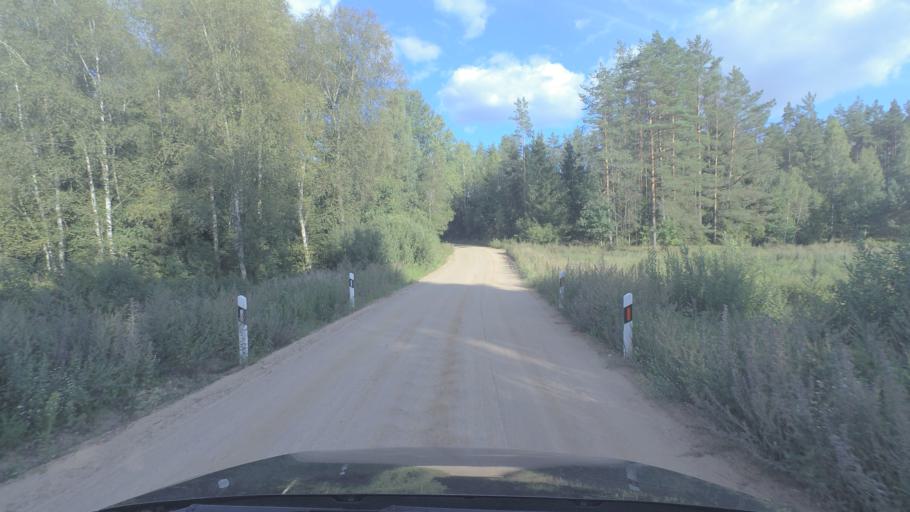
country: LT
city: Pabrade
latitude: 55.1481
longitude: 25.7545
